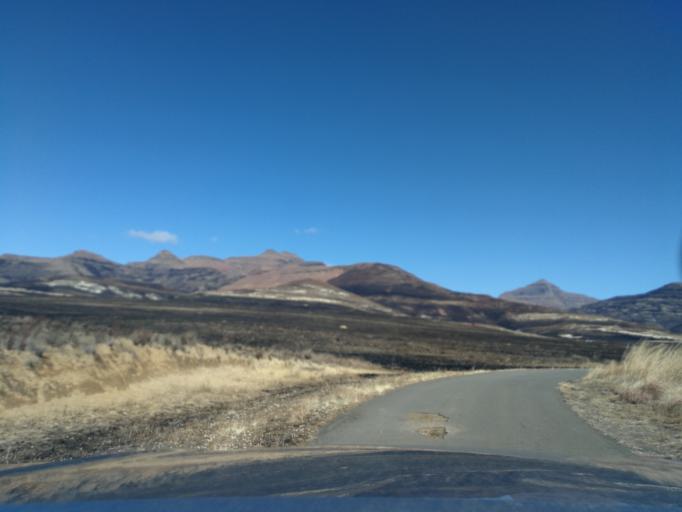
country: ZA
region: Orange Free State
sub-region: Thabo Mofutsanyana District Municipality
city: Phuthaditjhaba
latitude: -28.5121
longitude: 28.6230
